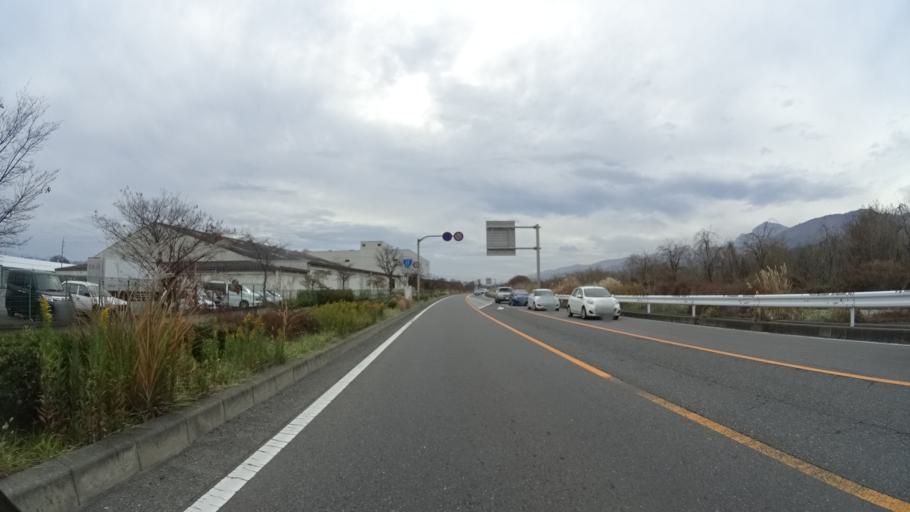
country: JP
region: Gunma
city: Numata
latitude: 36.6556
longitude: 139.0210
